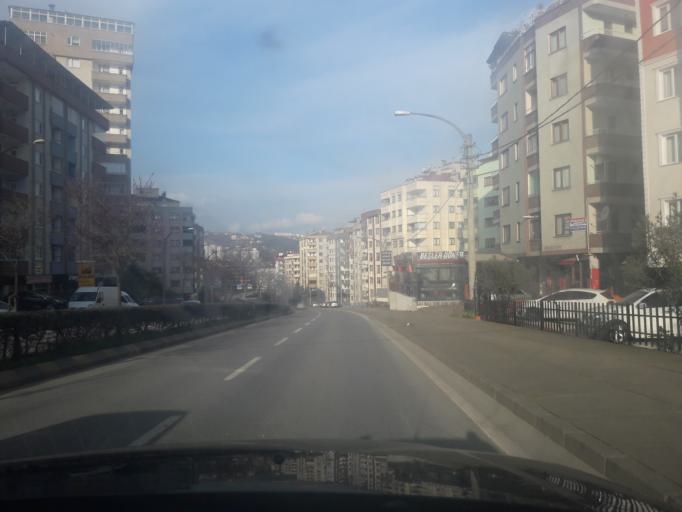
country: TR
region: Trabzon
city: Trabzon
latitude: 40.9965
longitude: 39.6813
